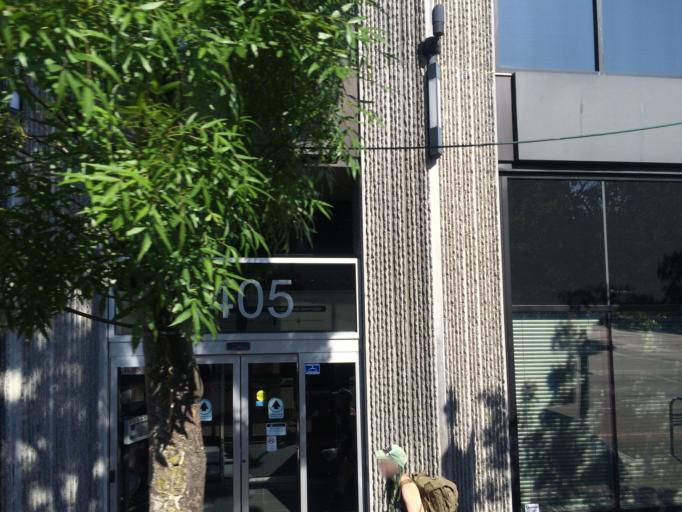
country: CA
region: British Columbia
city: Victoria
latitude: 48.4273
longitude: -123.3645
